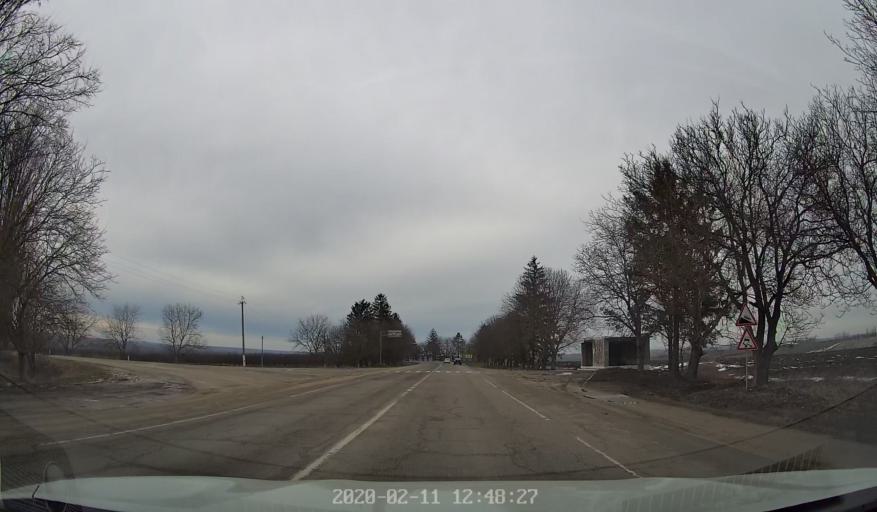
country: MD
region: Briceni
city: Briceni
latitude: 48.2814
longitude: 27.1480
